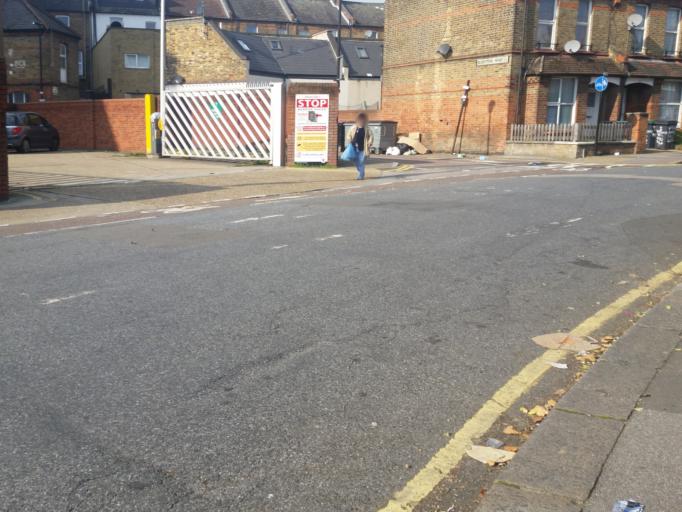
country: GB
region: England
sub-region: Greater London
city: Wood Green
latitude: 51.5954
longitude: -0.1077
